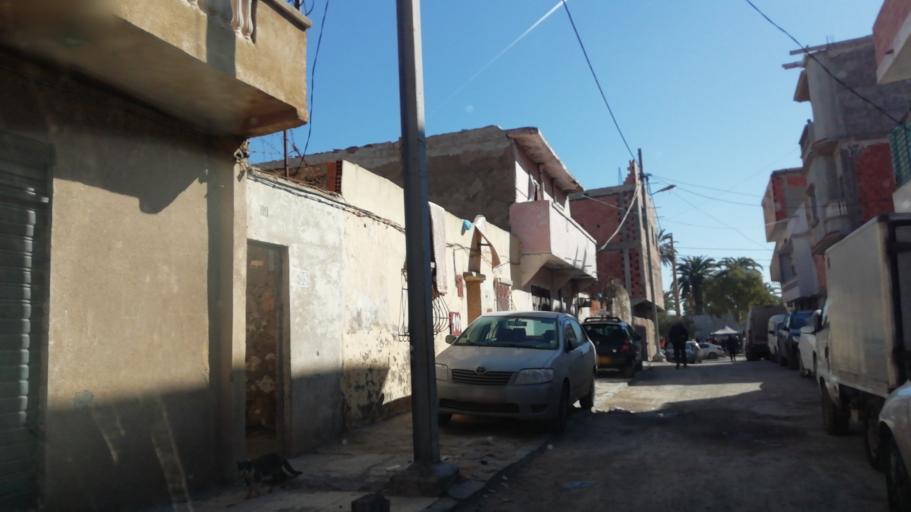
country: DZ
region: Oran
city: Oran
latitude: 35.6858
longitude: -0.6373
